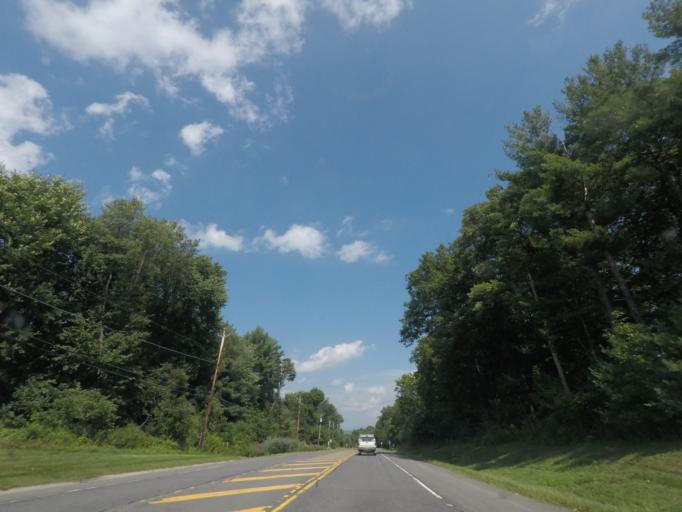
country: US
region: New York
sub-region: Rensselaer County
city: Poestenkill
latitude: 42.8077
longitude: -73.5446
